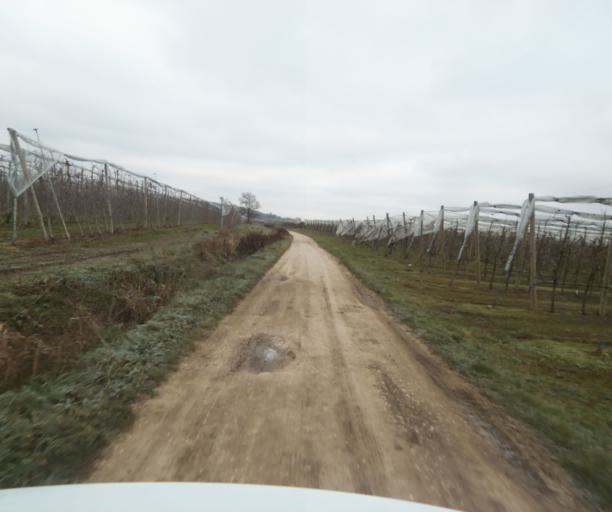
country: FR
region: Midi-Pyrenees
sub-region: Departement du Tarn-et-Garonne
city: Moissac
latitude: 44.1108
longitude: 1.1338
